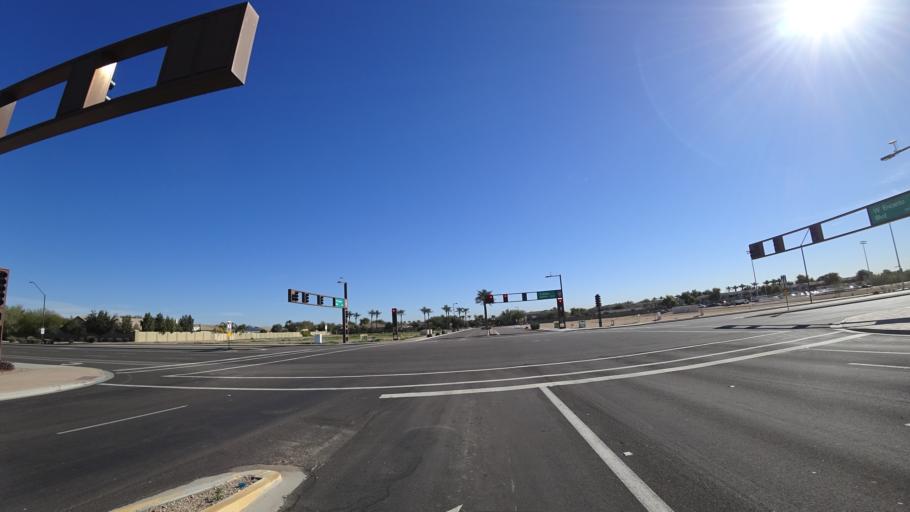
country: US
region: Arizona
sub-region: Maricopa County
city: Litchfield Park
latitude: 33.4717
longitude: -112.3758
